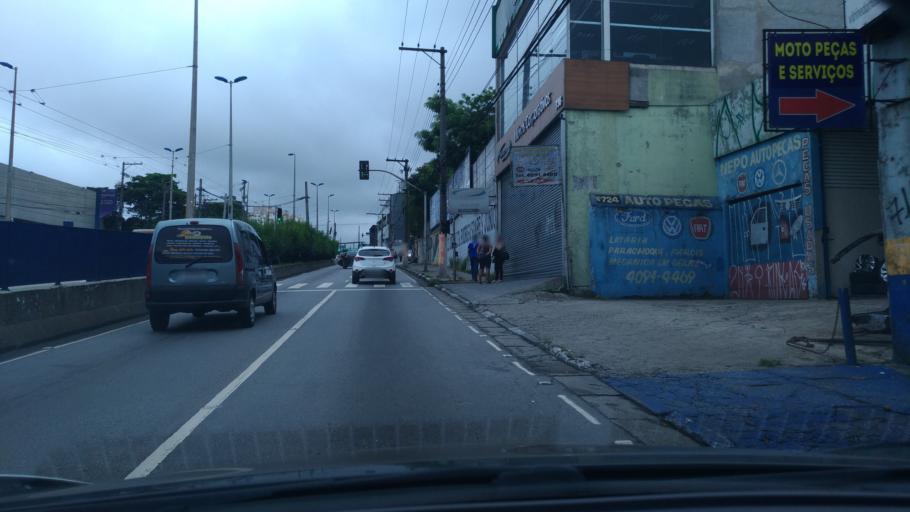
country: BR
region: Sao Paulo
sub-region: Sao Bernardo Do Campo
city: Sao Bernardo do Campo
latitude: -23.6862
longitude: -46.5931
